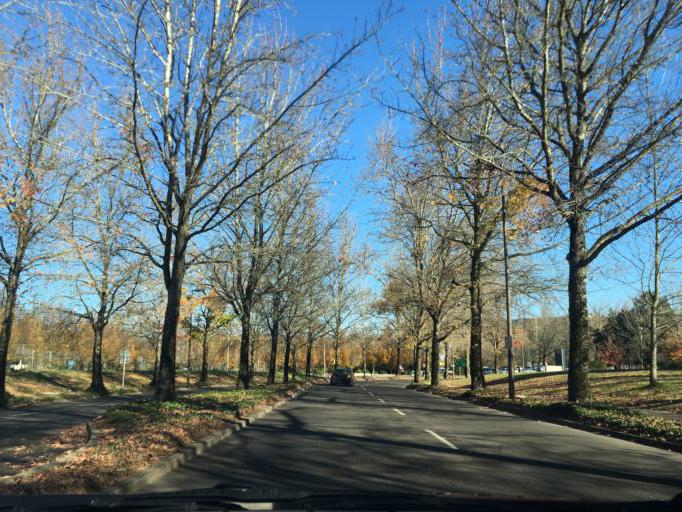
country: US
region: Oregon
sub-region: Multnomah County
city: Portland
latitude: 45.5462
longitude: -122.6708
